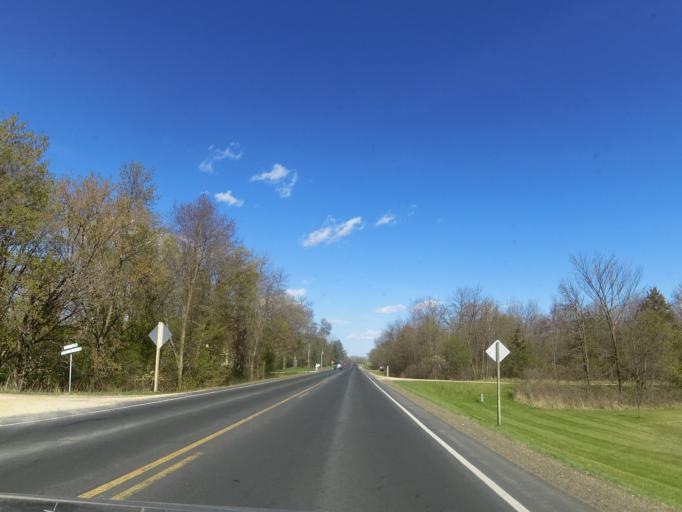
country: US
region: Minnesota
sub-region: Washington County
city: Bayport
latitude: 45.0573
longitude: -92.7381
